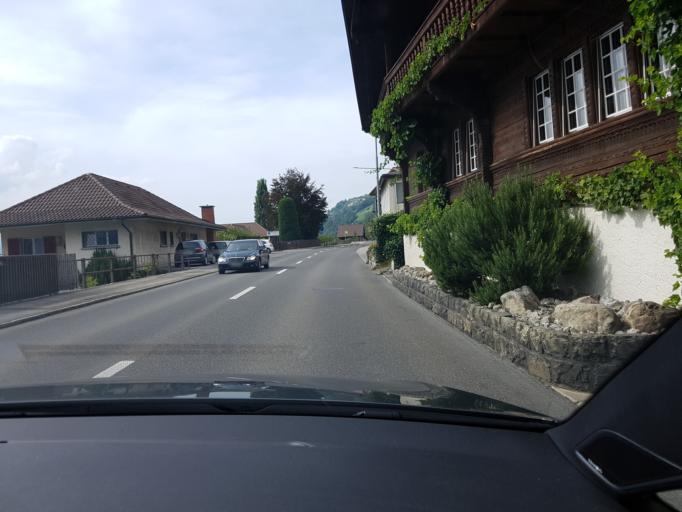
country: CH
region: Bern
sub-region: Thun District
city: Sigriswil
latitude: 46.7012
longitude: 7.7340
